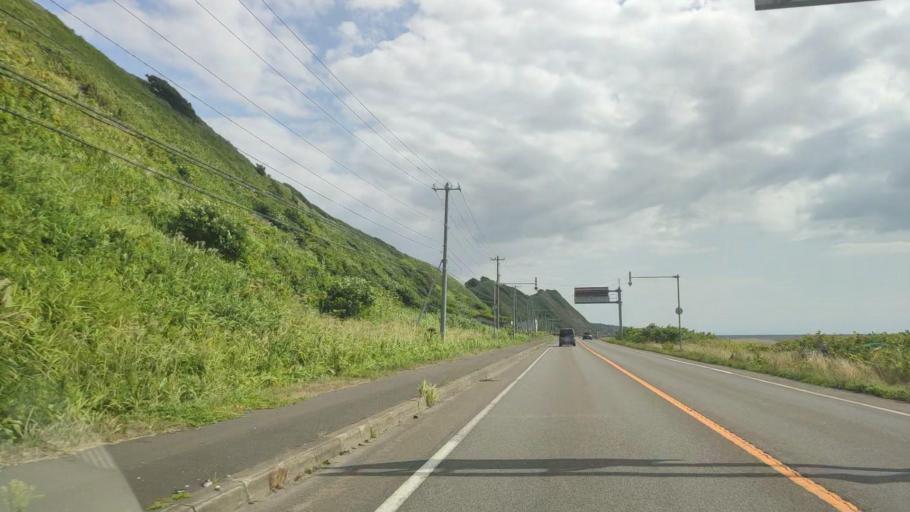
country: JP
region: Hokkaido
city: Rumoi
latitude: 44.2199
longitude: 141.6554
